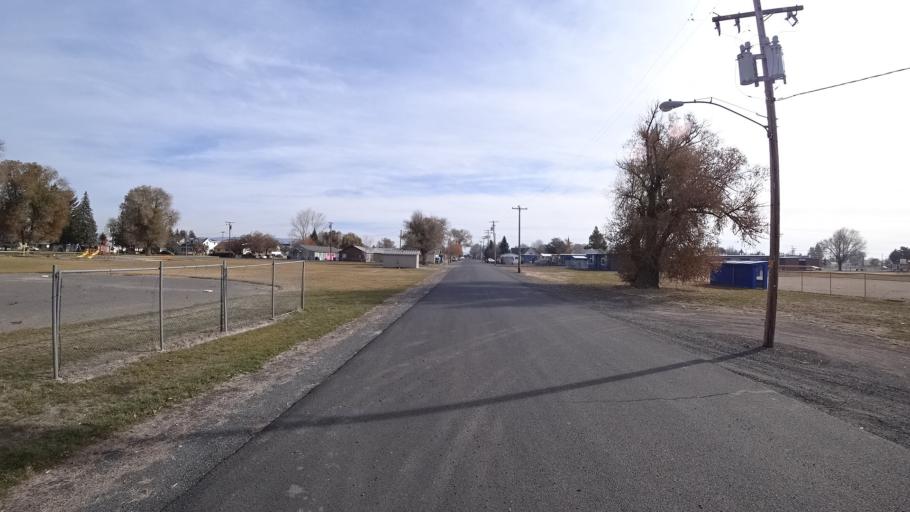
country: US
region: California
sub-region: Siskiyou County
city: Tulelake
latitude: 41.9560
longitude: -121.4804
